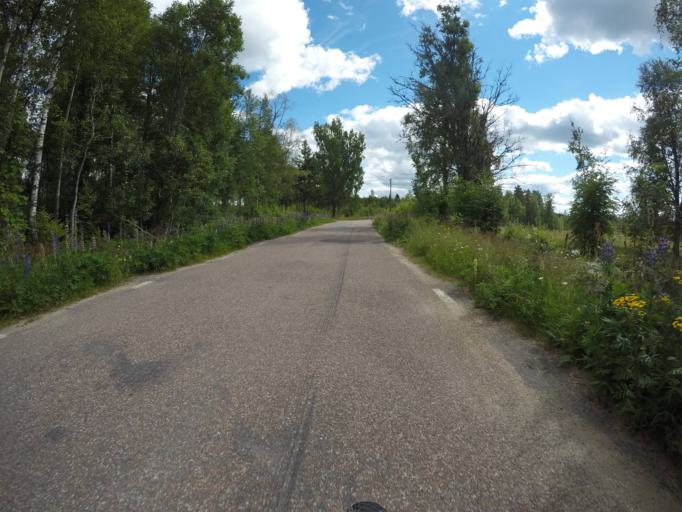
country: SE
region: OErebro
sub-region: Hallefors Kommun
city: Haellefors
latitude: 60.0499
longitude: 14.5036
